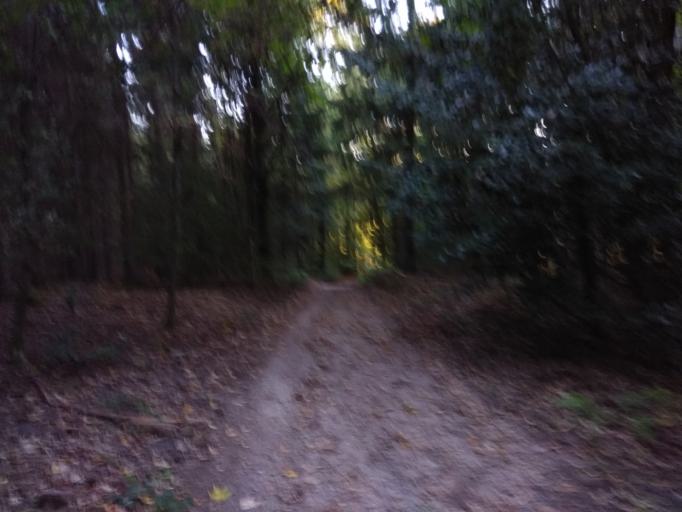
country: DE
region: Baden-Wuerttemberg
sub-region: Karlsruhe Region
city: Heidelberg
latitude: 49.4081
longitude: 8.7283
